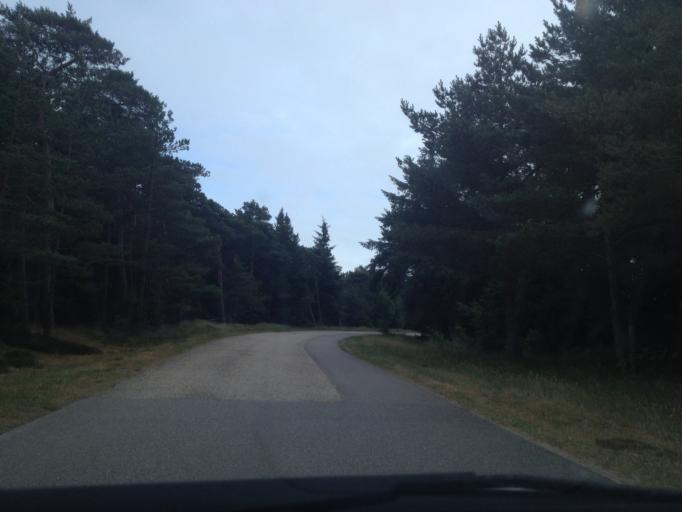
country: DK
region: South Denmark
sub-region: Varde Kommune
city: Oksbol
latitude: 55.5337
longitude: 8.2251
